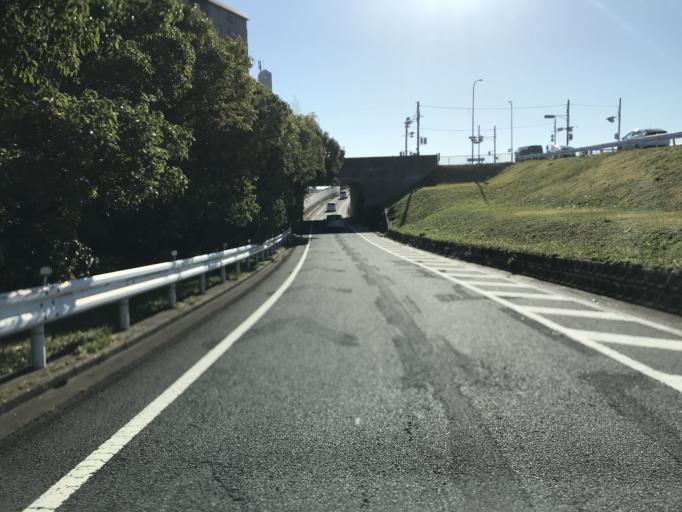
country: JP
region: Aichi
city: Kanie
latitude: 35.1696
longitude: 136.8374
